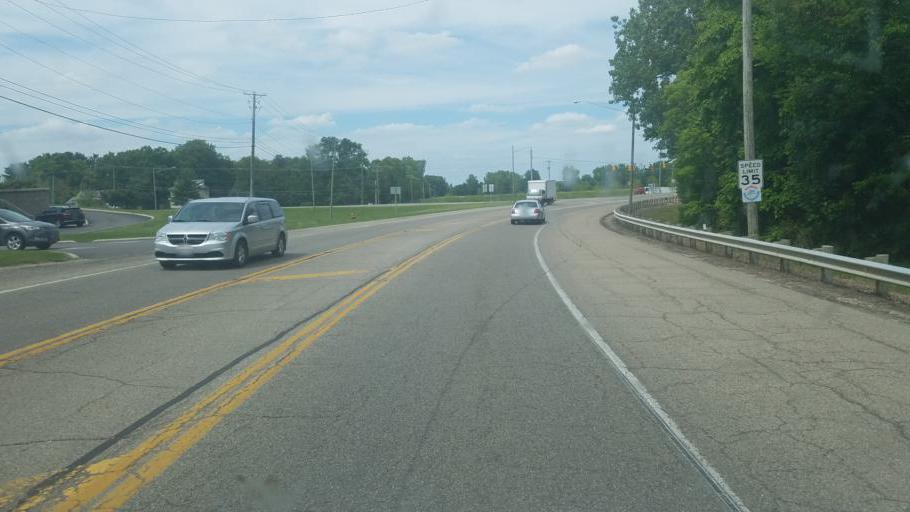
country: US
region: Ohio
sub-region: Knox County
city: Mount Vernon
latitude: 40.3926
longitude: -82.5074
